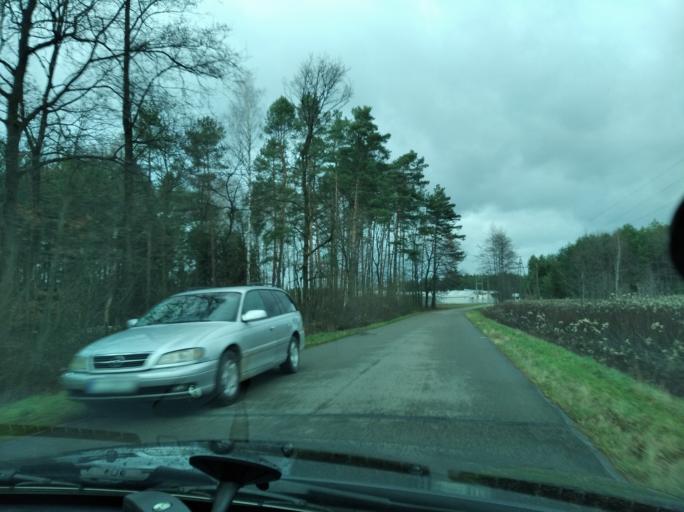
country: PL
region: Subcarpathian Voivodeship
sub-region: Powiat lancucki
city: Zolynia
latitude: 50.1332
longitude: 22.2828
